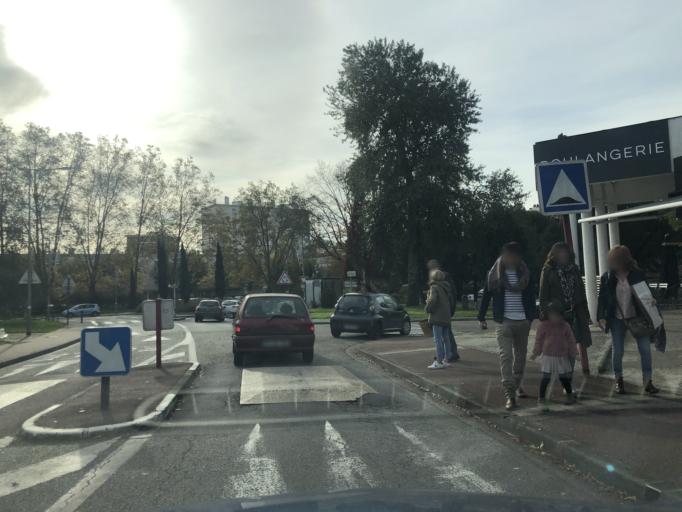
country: FR
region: Aquitaine
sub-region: Departement de la Gironde
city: Merignac
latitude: 44.8419
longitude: -0.6511
